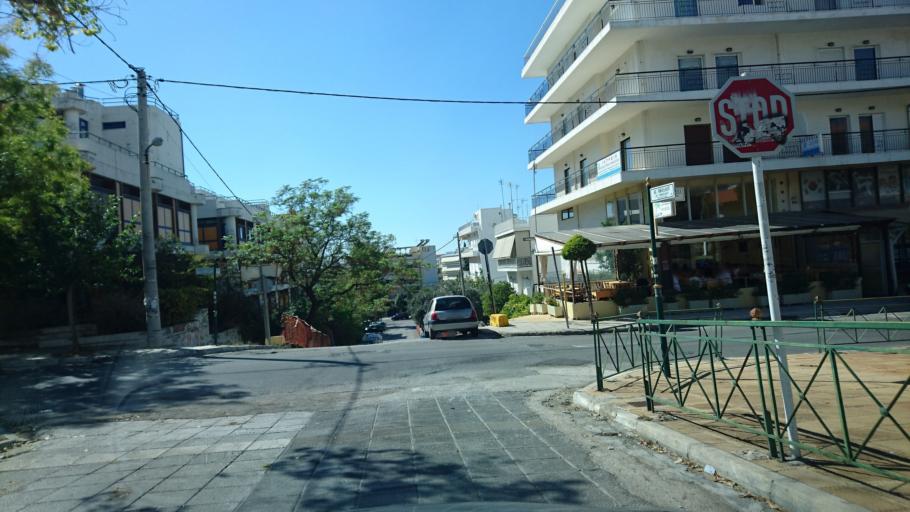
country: GR
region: Attica
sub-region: Nomarchia Athinas
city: Ilioupoli
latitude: 37.9357
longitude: 23.7529
